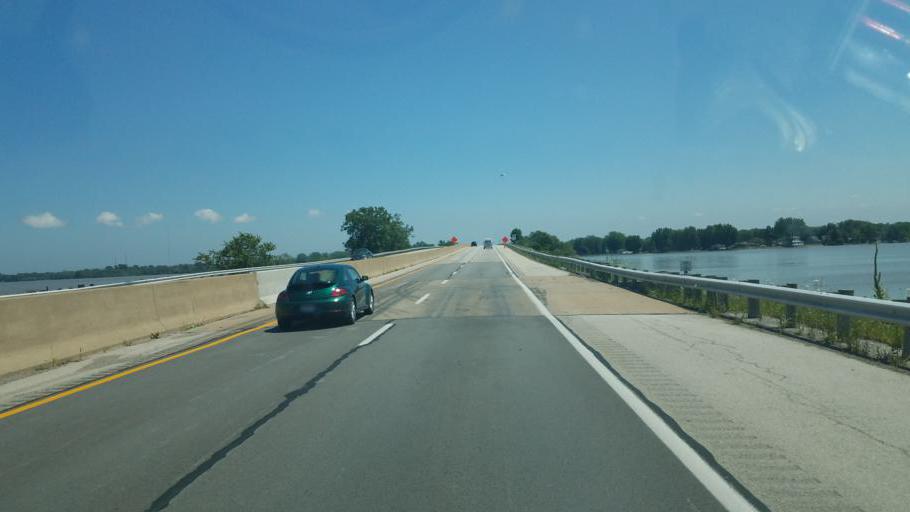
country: US
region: Ohio
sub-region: Ottawa County
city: Port Clinton
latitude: 41.5149
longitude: -82.9948
